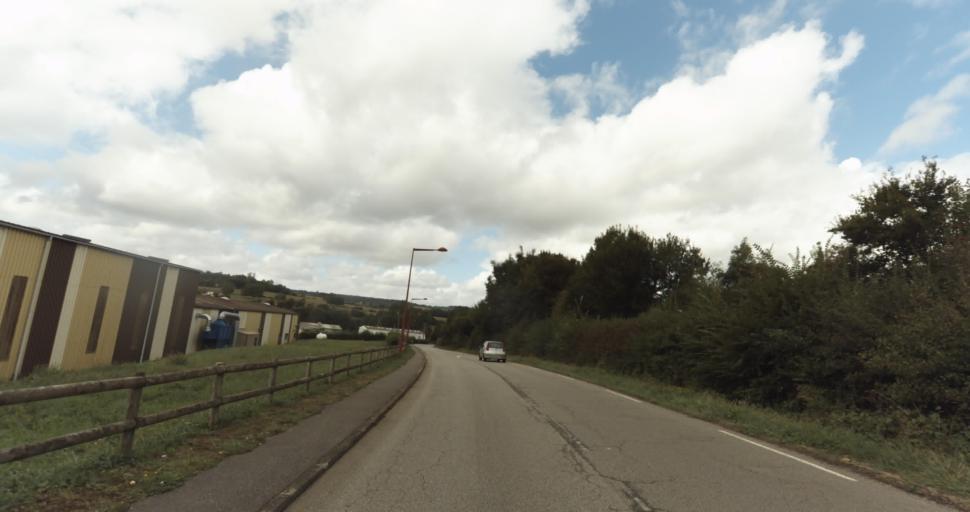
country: FR
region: Lower Normandy
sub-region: Departement de l'Orne
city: Gace
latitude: 48.7980
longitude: 0.2941
